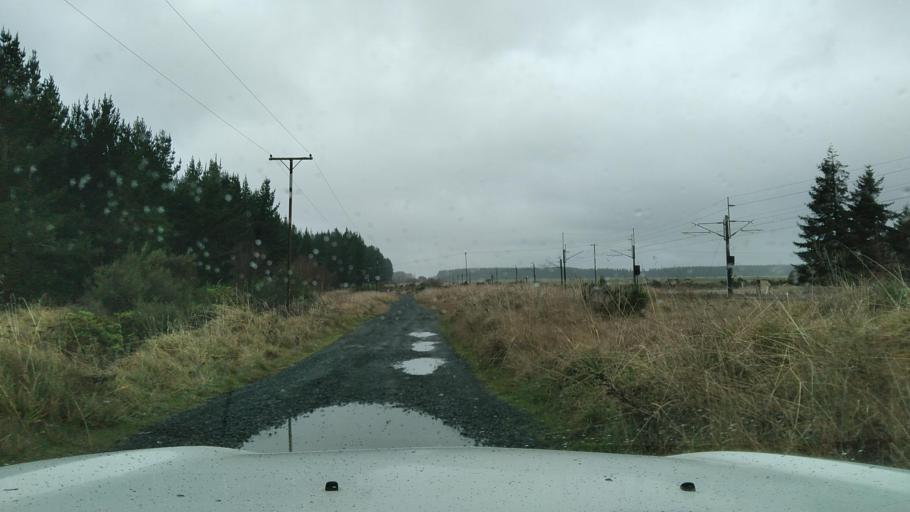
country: NZ
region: Manawatu-Wanganui
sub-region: Ruapehu District
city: Waiouru
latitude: -39.4474
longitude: 175.5129
